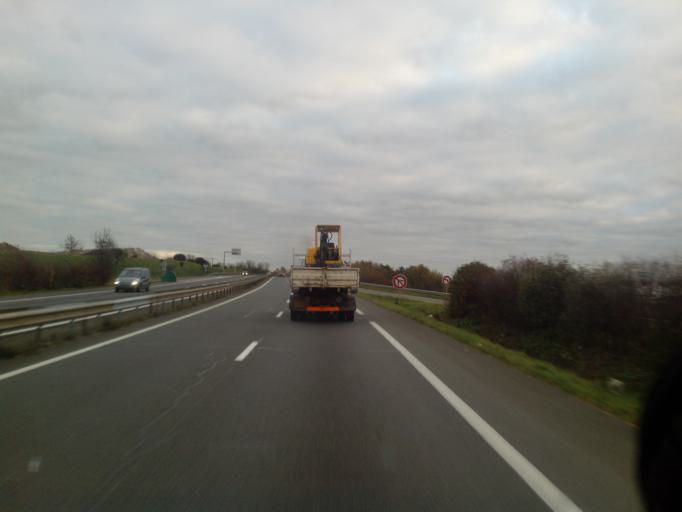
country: FR
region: Poitou-Charentes
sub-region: Departement de la Vienne
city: Montamise
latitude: 46.6107
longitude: 0.3895
